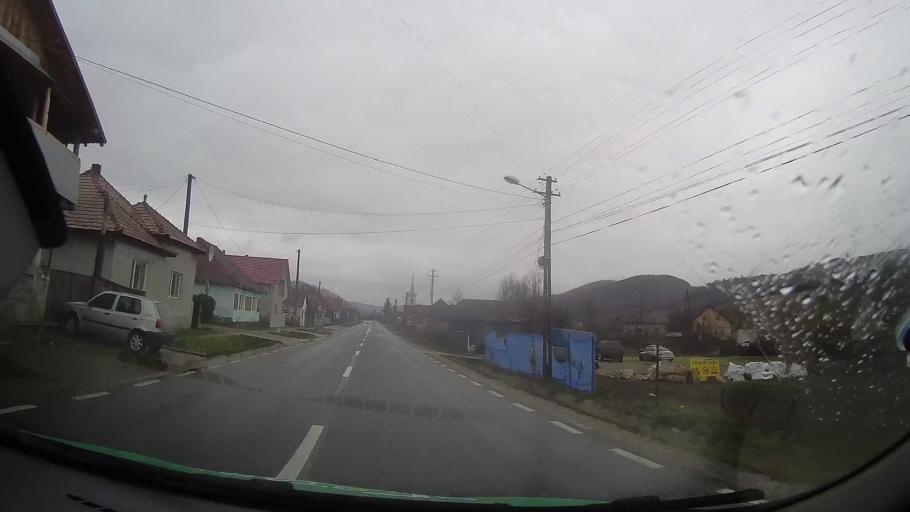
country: RO
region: Bistrita-Nasaud
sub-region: Comuna Galatii Bistritei
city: Galatii Bistritei
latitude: 46.9486
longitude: 24.4536
